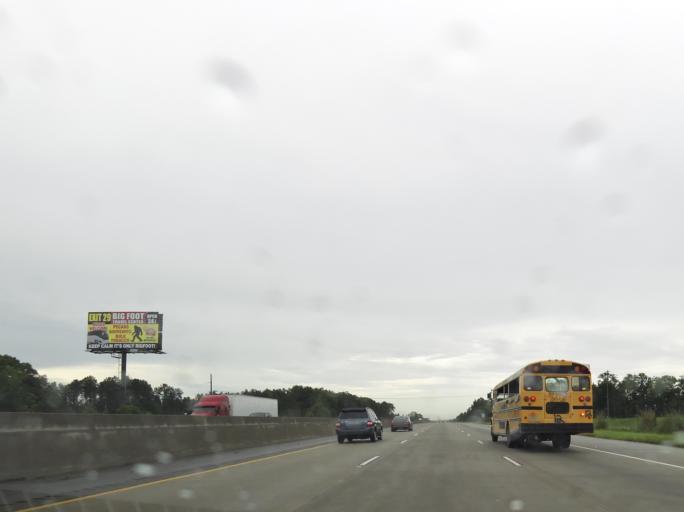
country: US
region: Georgia
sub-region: Cook County
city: Adel
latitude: 31.1009
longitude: -83.4216
